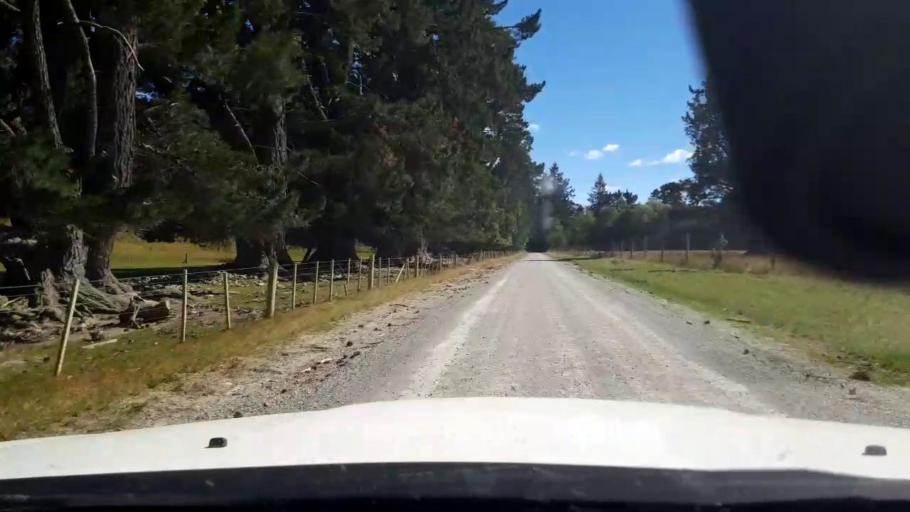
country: NZ
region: Canterbury
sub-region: Timaru District
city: Pleasant Point
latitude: -44.0282
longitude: 170.7435
